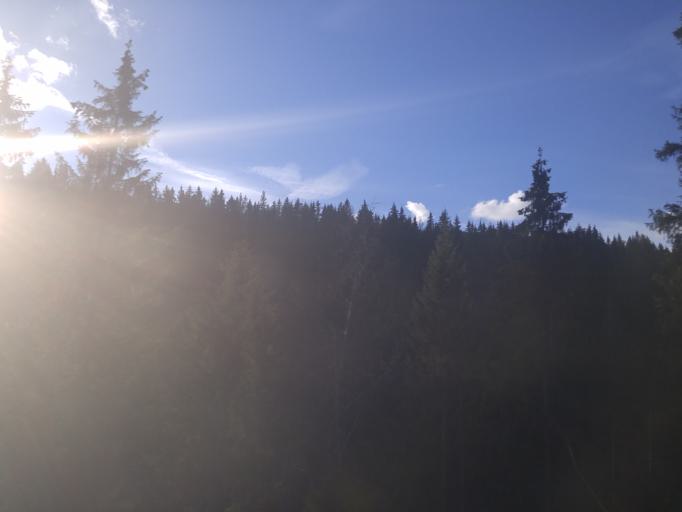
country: NO
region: Oppland
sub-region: Lillehammer
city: Lillehammer
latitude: 61.1949
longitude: 10.4101
